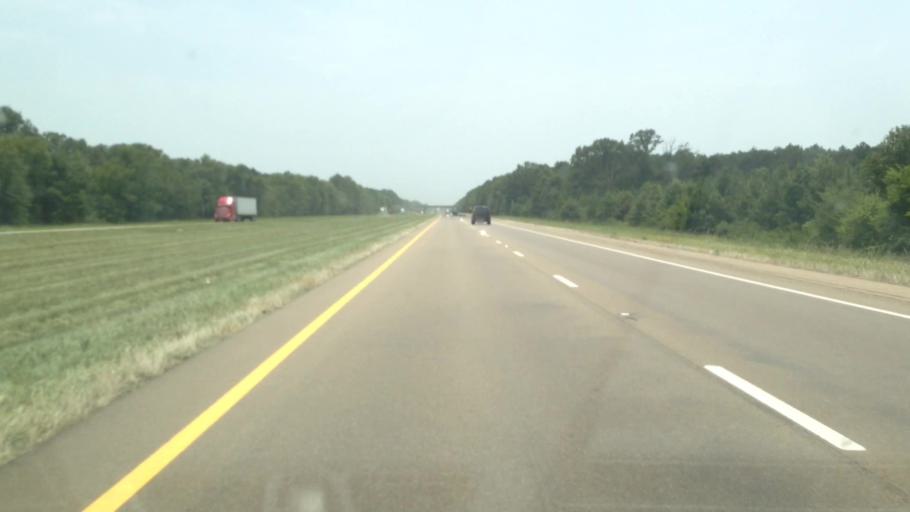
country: US
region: Texas
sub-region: Morris County
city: Naples
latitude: 33.3411
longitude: -94.6622
